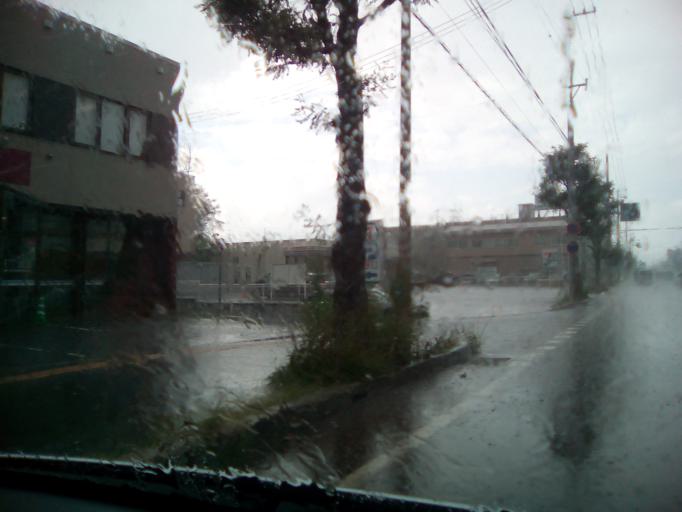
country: JP
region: Hokkaido
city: Sapporo
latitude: 43.0434
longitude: 141.4201
